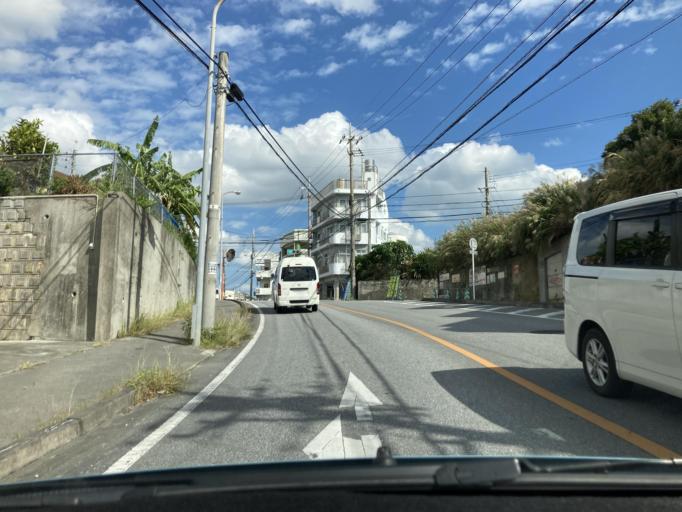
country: JP
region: Okinawa
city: Chatan
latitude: 26.3186
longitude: 127.7783
